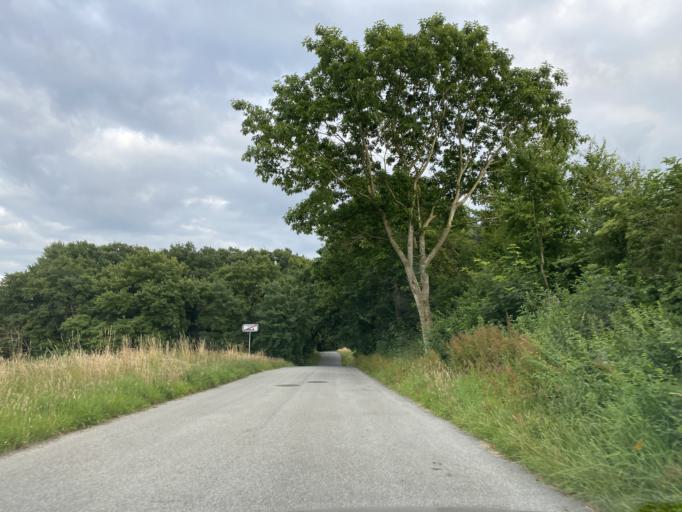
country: DK
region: Central Jutland
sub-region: Favrskov Kommune
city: Hammel
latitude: 56.2215
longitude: 9.7482
